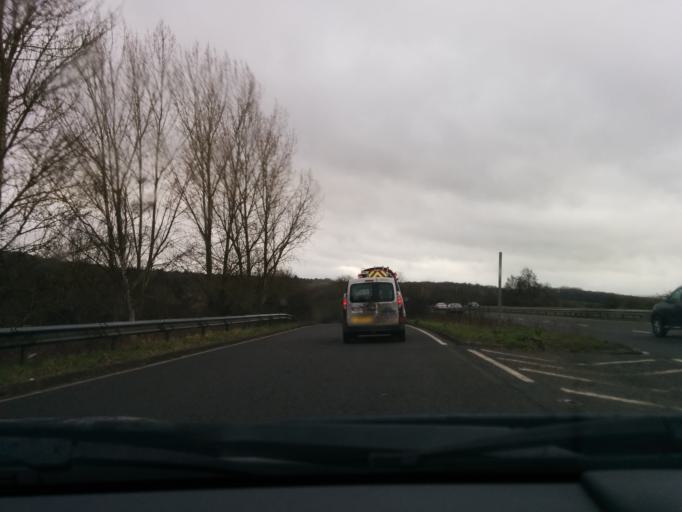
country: GB
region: England
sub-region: Oxfordshire
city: Boars Hill
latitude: 51.7521
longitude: -1.3140
